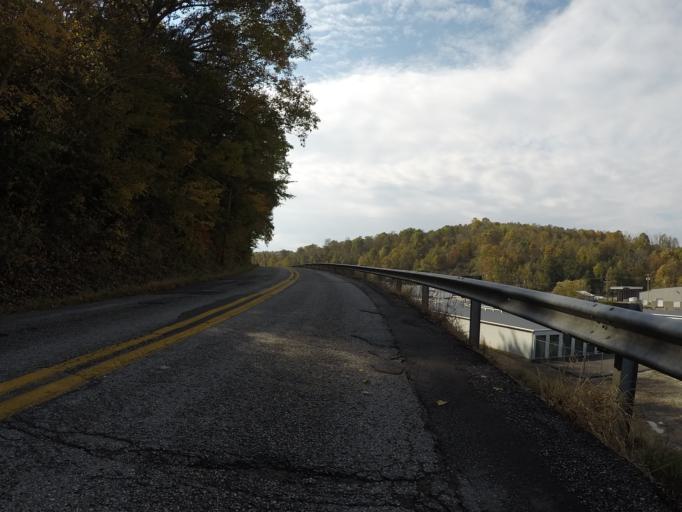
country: US
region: West Virginia
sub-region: Cabell County
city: Huntington
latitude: 38.3855
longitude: -82.3947
